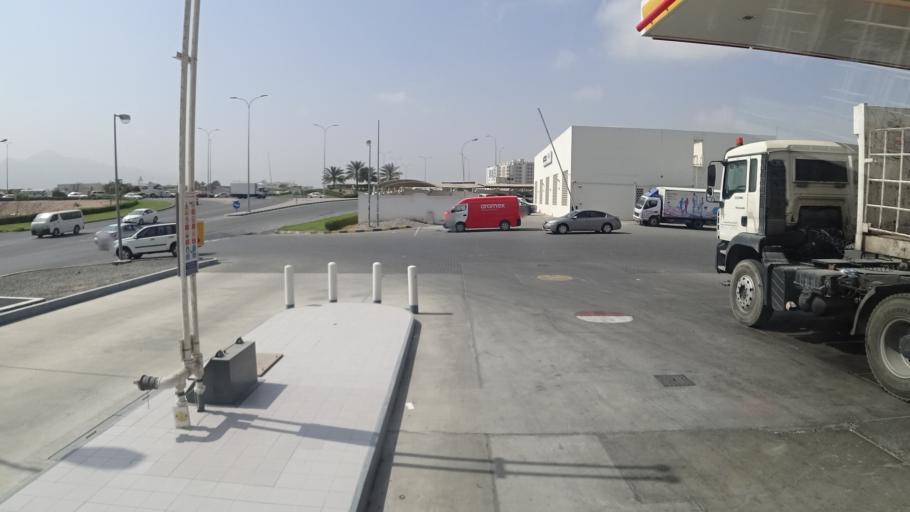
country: OM
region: Muhafazat Masqat
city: Bawshar
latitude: 23.5842
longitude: 58.3601
